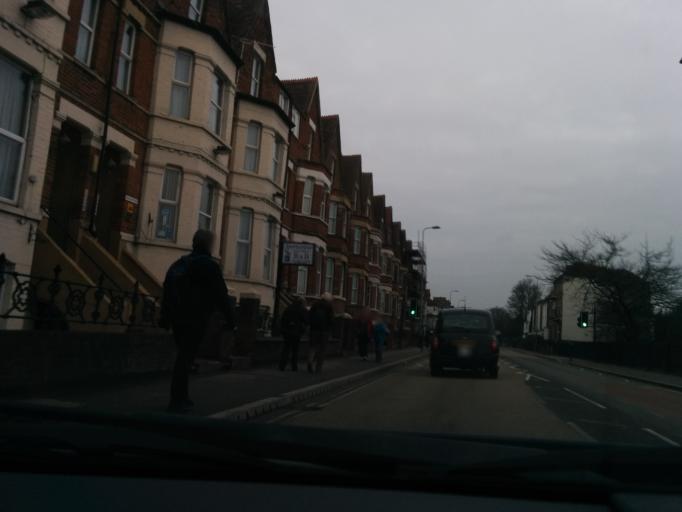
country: GB
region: England
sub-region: Oxfordshire
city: Oxford
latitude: 51.7417
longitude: -1.2548
